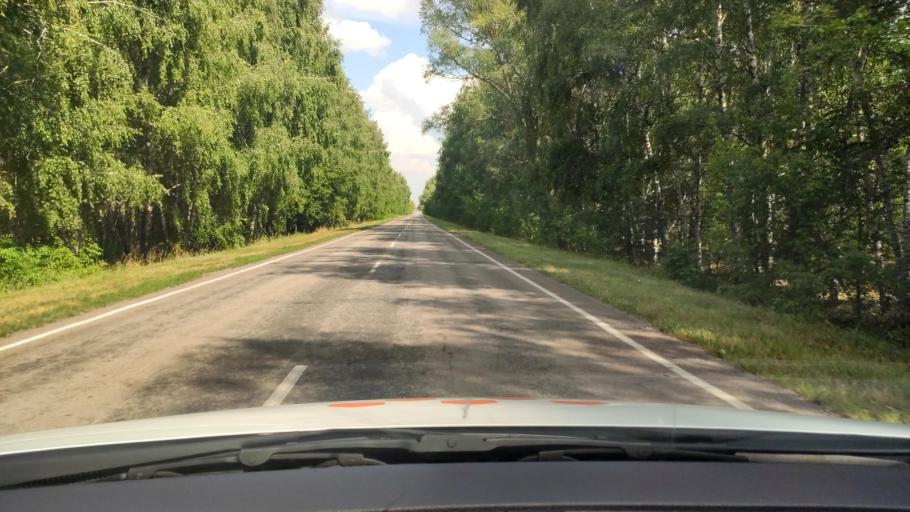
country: RU
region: Voronezj
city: Sadovoye
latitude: 51.7824
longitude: 40.5546
